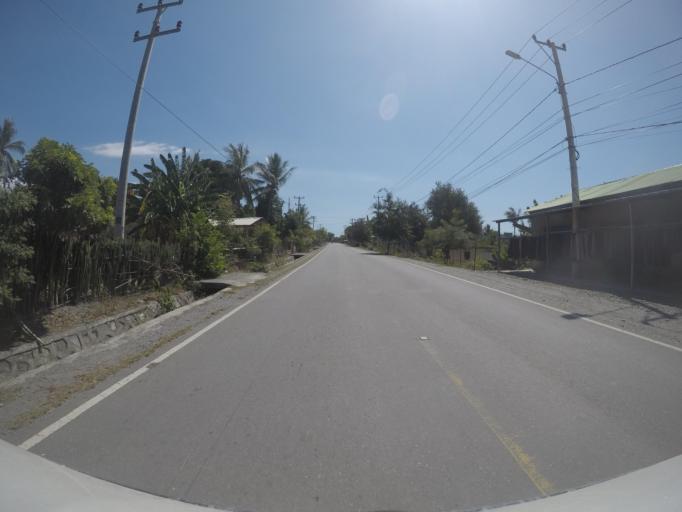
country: TL
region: Liquica
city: Liquica
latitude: -8.5894
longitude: 125.3455
